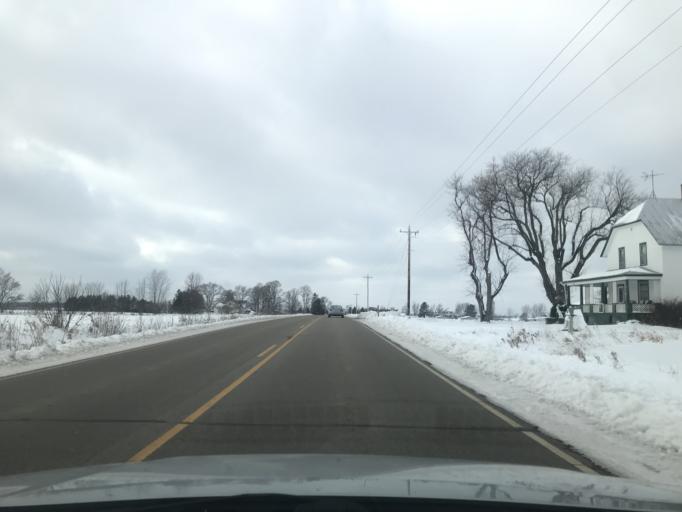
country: US
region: Wisconsin
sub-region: Oconto County
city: Oconto
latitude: 44.9499
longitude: -87.9121
